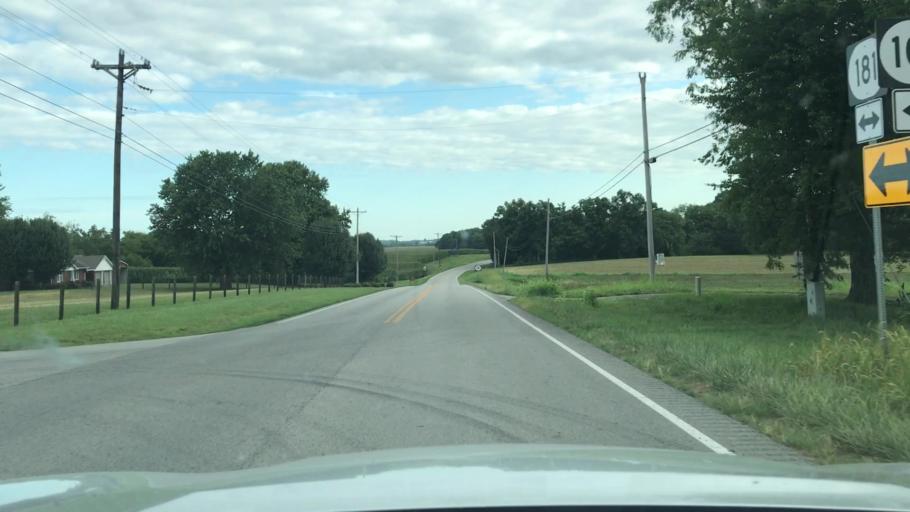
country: US
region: Kentucky
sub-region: Todd County
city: Elkton
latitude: 36.7874
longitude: -87.1640
